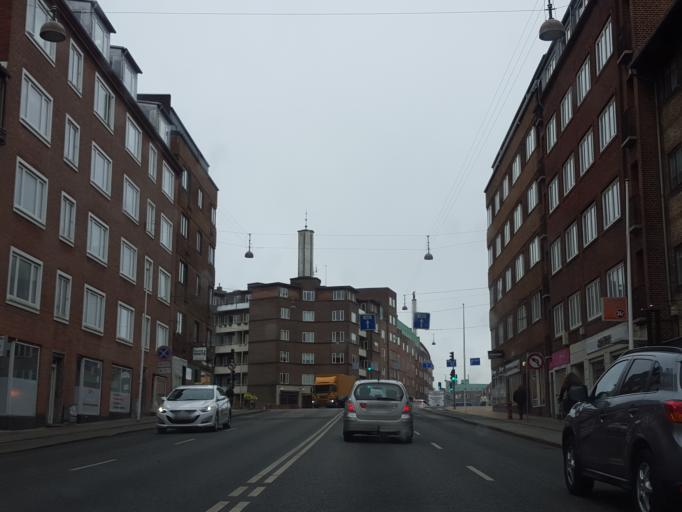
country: DK
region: North Denmark
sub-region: Alborg Kommune
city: Aalborg
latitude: 57.0456
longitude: 9.9128
